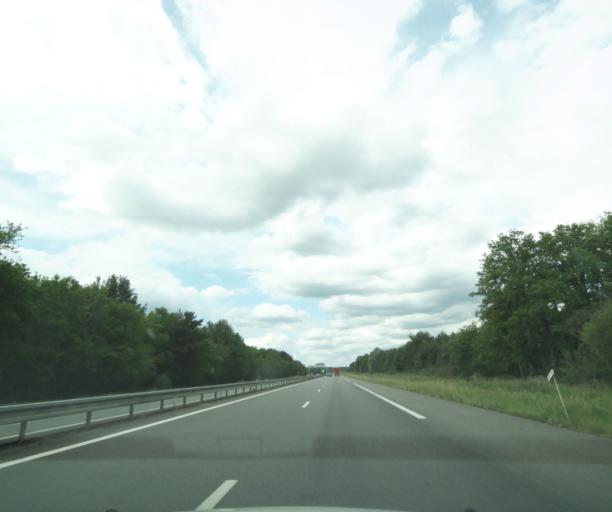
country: FR
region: Centre
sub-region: Departement du Loir-et-Cher
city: Theillay
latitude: 47.3227
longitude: 2.0495
